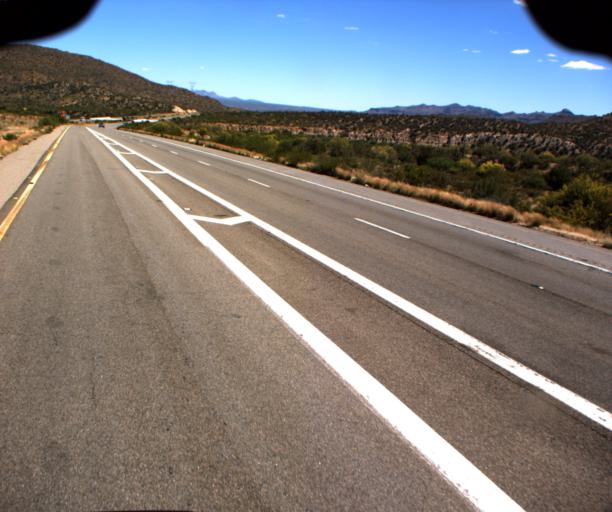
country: US
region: Arizona
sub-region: Yavapai County
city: Bagdad
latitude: 34.4275
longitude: -113.2459
